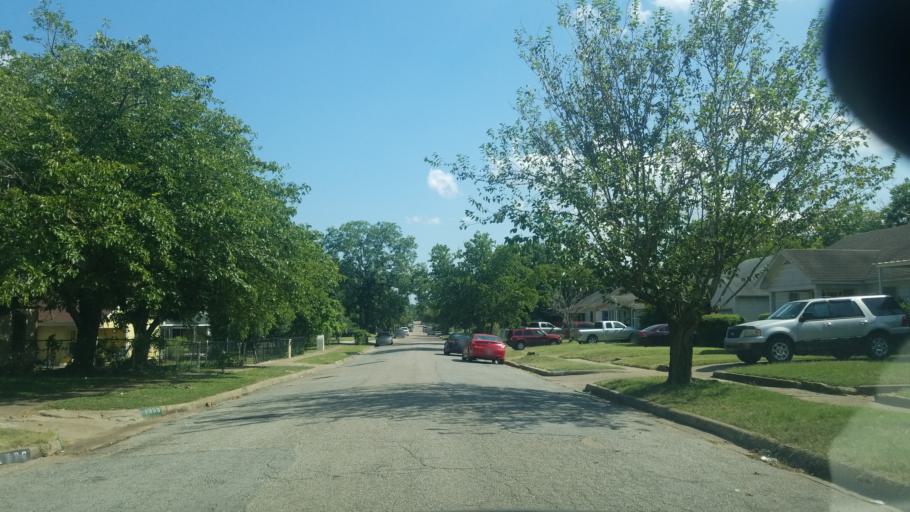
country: US
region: Texas
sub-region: Dallas County
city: Dallas
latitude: 32.7322
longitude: -96.8103
